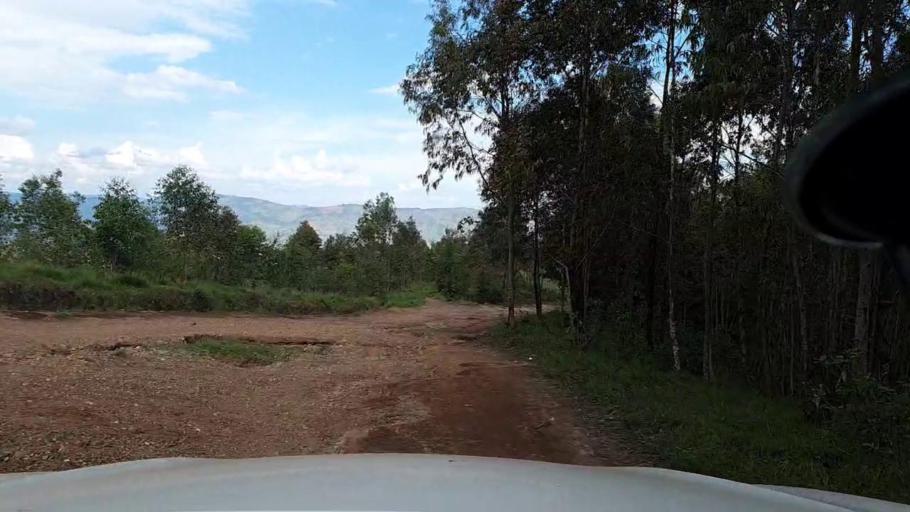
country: RW
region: Kigali
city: Kigali
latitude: -1.7822
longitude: 29.8358
